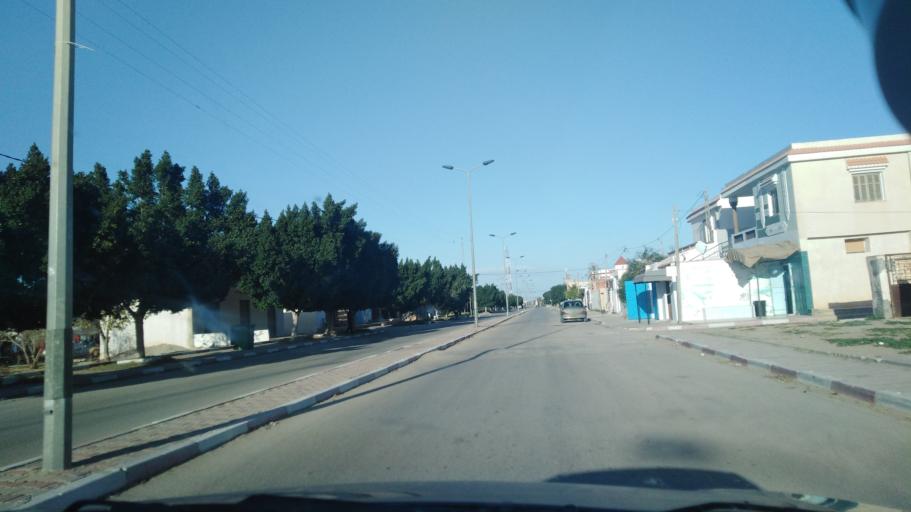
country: TN
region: Al Mahdiyah
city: Shurban
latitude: 34.9668
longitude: 10.3685
